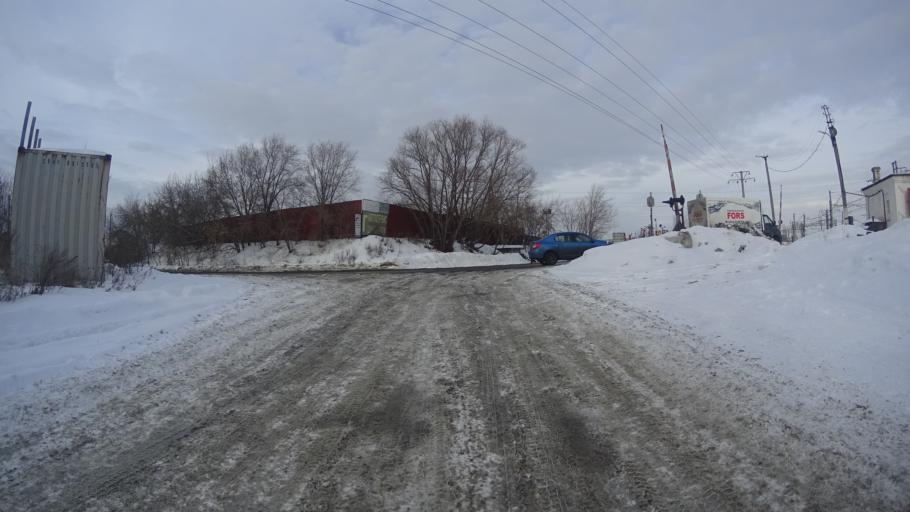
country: RU
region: Chelyabinsk
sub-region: Gorod Chelyabinsk
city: Chelyabinsk
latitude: 55.1280
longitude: 61.4025
